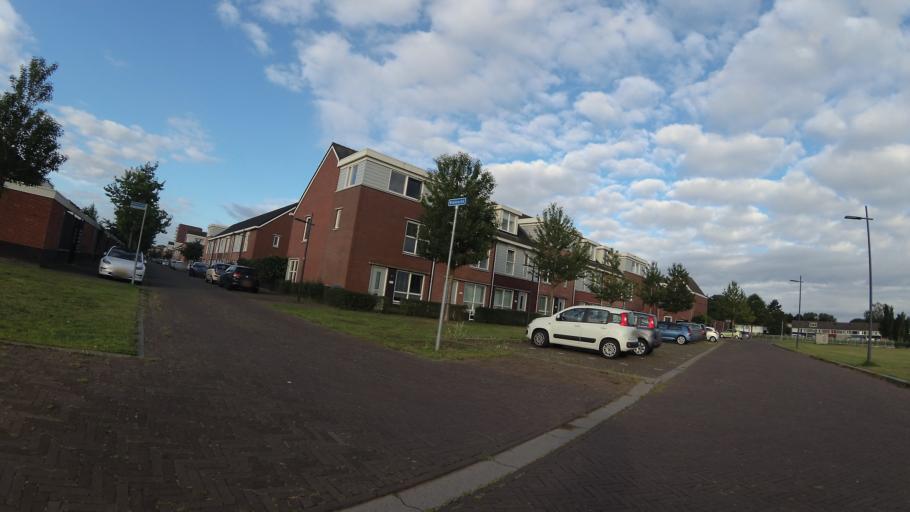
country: NL
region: North Brabant
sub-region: Gemeente Breda
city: Hoge Vucht
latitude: 51.6114
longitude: 4.8044
